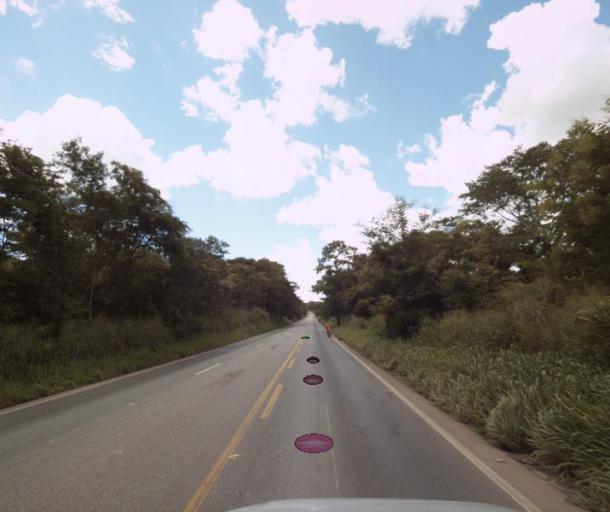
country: BR
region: Goias
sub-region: Porangatu
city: Porangatu
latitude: -13.7672
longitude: -49.0295
